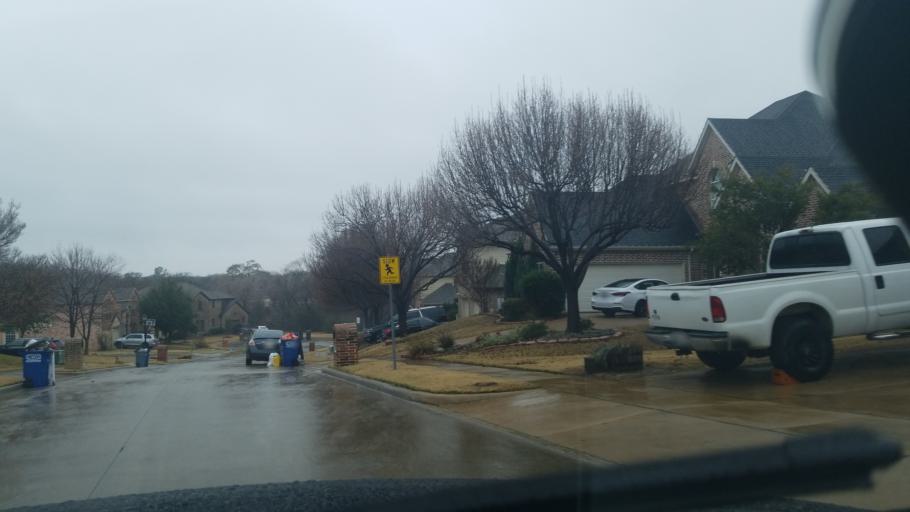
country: US
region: Texas
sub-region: Denton County
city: Corinth
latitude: 33.1360
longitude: -97.0917
